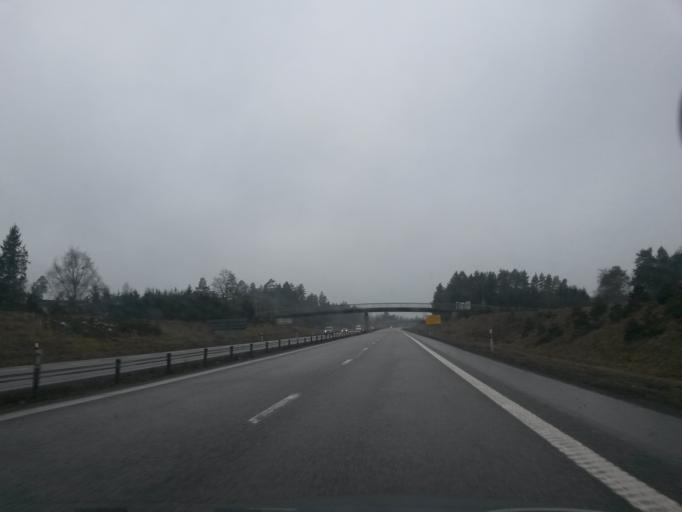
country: SE
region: Vaestra Goetaland
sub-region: Trollhattan
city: Trollhattan
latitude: 58.3365
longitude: 12.2276
